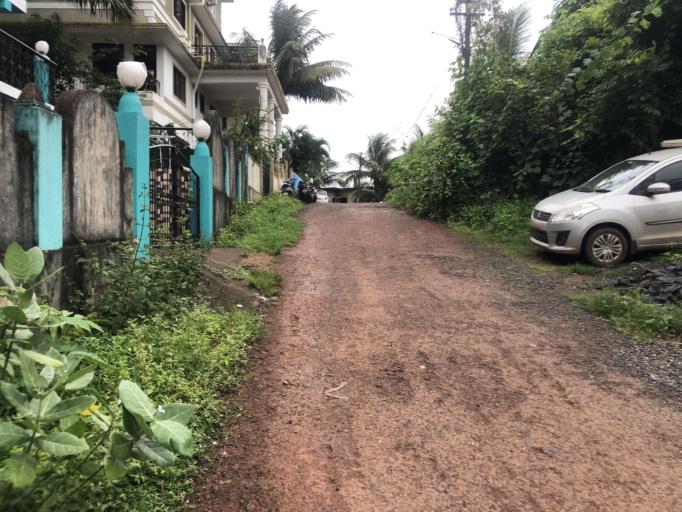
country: IN
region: Goa
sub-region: North Goa
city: Serula
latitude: 15.5491
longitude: 73.8289
